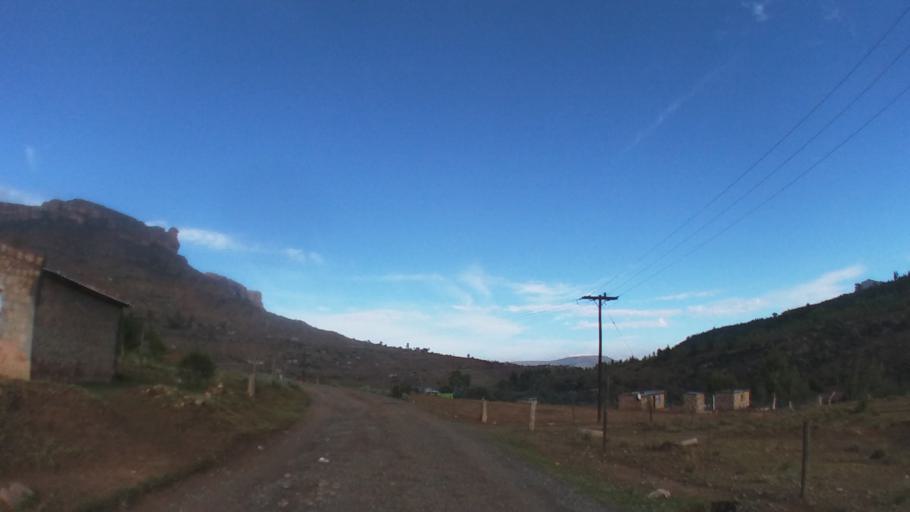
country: LS
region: Maseru
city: Maseru
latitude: -29.4026
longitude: 27.4713
